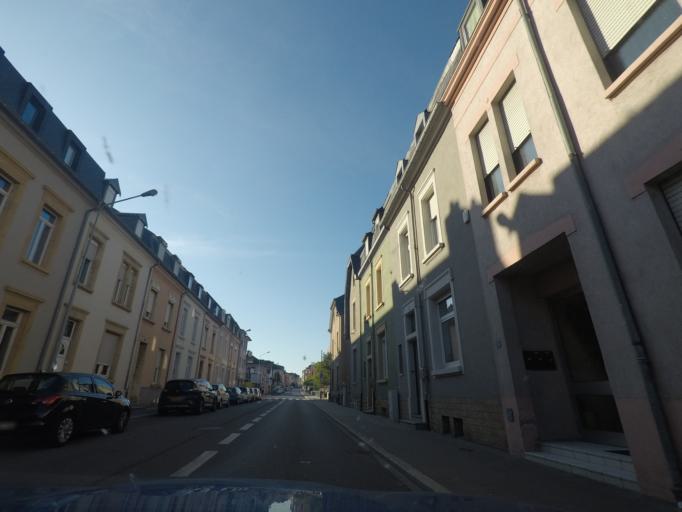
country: LU
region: Luxembourg
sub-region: Canton de Luxembourg
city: Luxembourg
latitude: 49.5950
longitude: 6.1403
